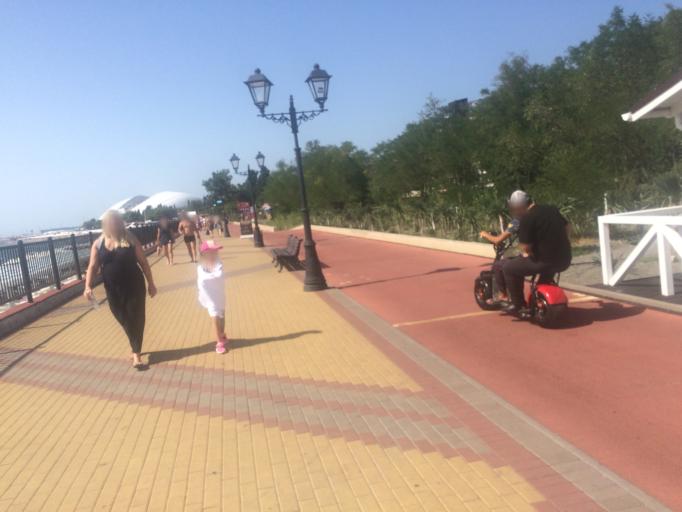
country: RU
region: Krasnodarskiy
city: Adler
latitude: 43.3956
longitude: 39.9721
